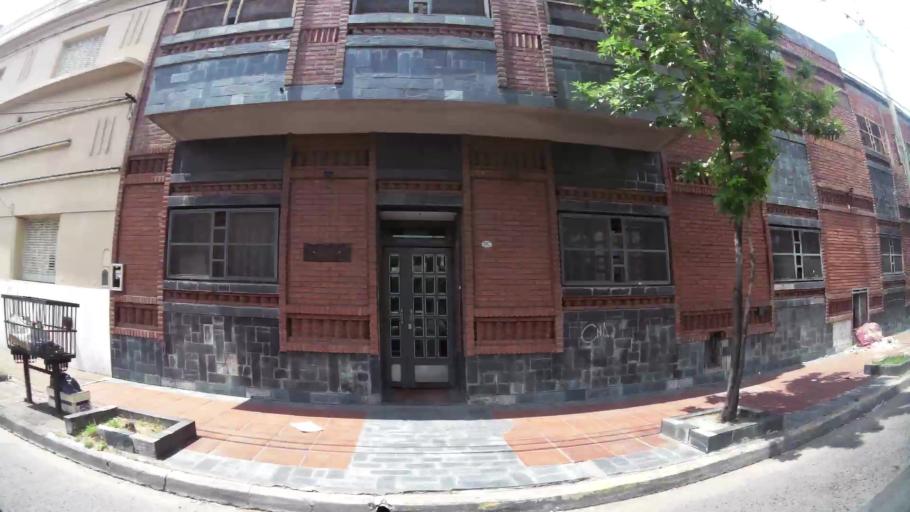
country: AR
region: Buenos Aires
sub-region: Partido de Lanus
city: Lanus
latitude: -34.6671
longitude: -58.4173
